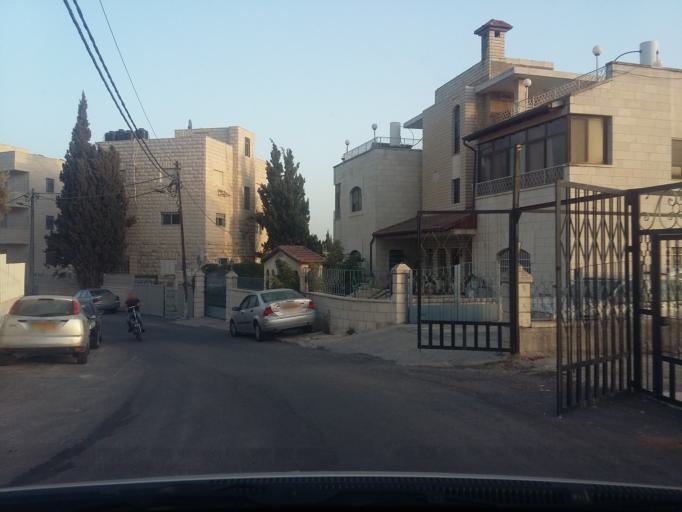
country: PS
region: West Bank
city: East Jerusalem
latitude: 31.7904
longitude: 35.2367
